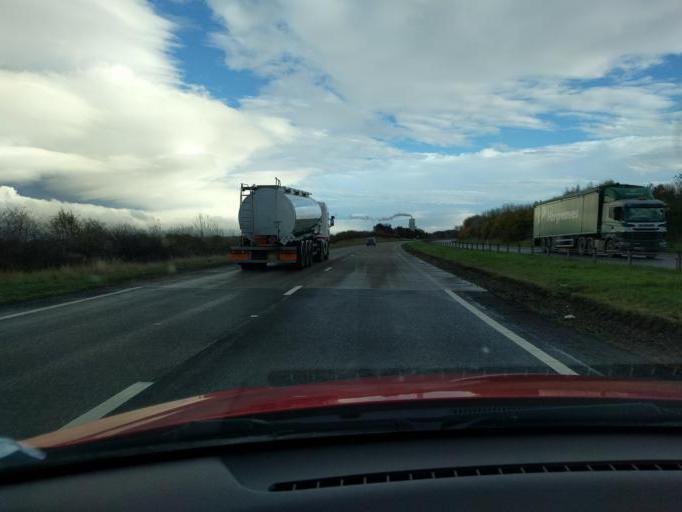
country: GB
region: Scotland
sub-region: East Lothian
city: Dunbar
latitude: 55.9870
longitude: -2.5014
